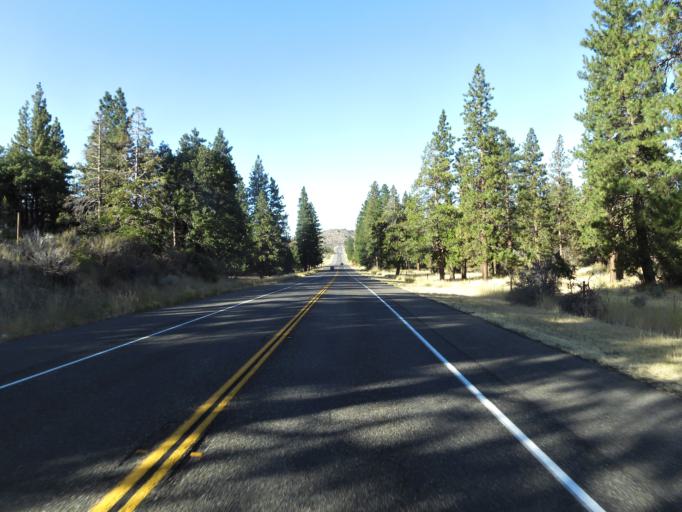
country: US
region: California
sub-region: Siskiyou County
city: Weed
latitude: 41.4630
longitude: -122.3552
